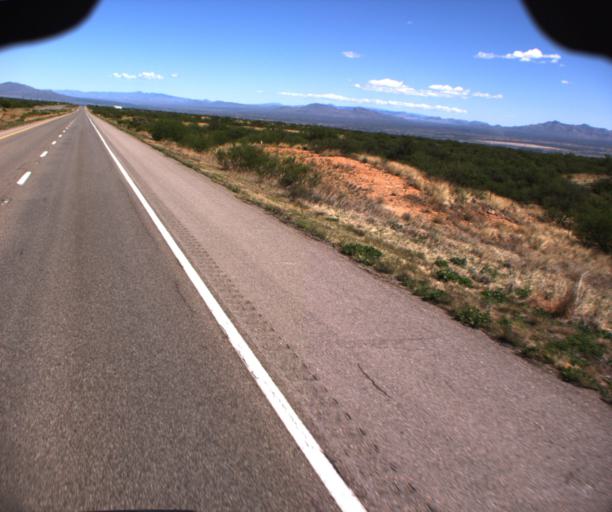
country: US
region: Arizona
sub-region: Cochise County
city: Whetstone
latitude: 31.8947
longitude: -110.3410
